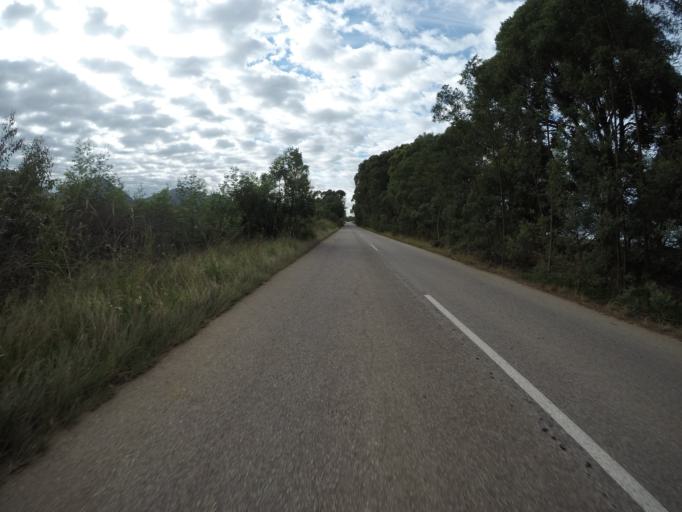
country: ZA
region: Eastern Cape
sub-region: Cacadu District Municipality
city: Kareedouw
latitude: -34.0449
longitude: 24.4409
